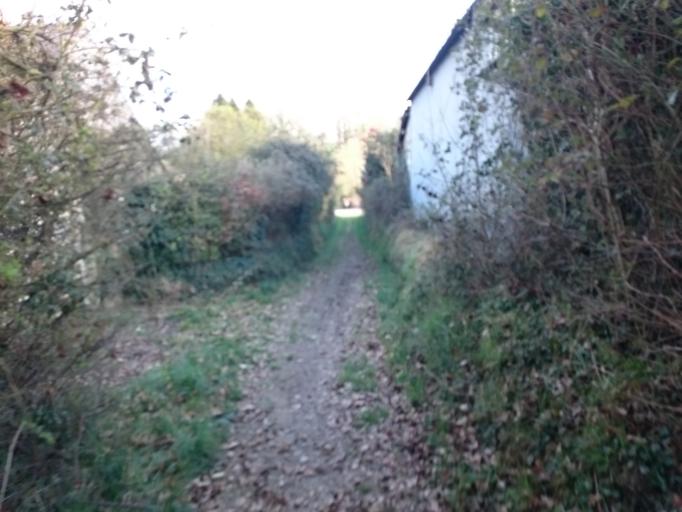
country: FR
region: Brittany
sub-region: Departement d'Ille-et-Vilaine
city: Chanteloup
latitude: 47.9358
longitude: -1.6093
